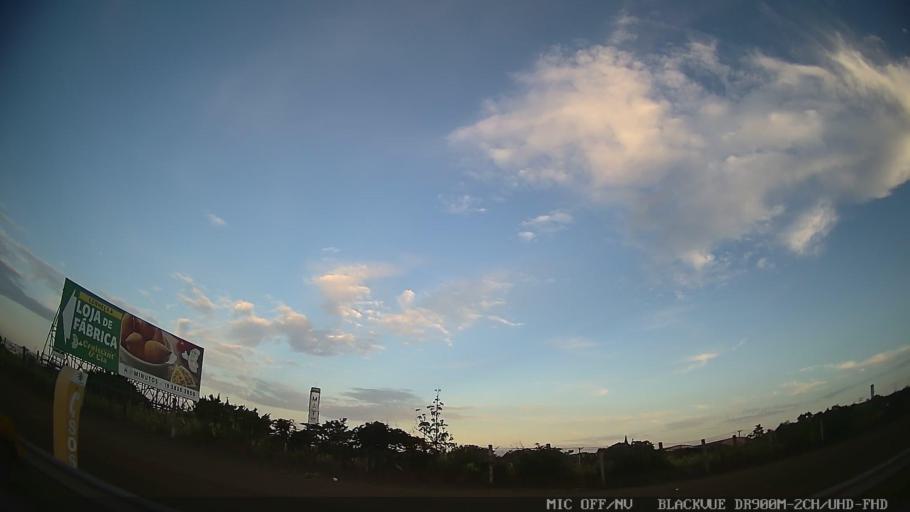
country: BR
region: Sao Paulo
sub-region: Indaiatuba
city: Indaiatuba
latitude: -23.1393
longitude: -47.2444
